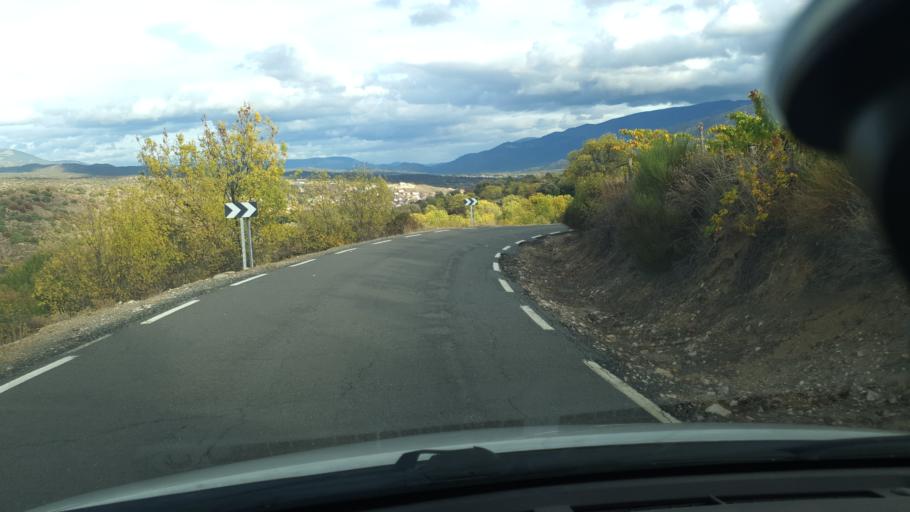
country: ES
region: Castille and Leon
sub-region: Provincia de Avila
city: Burgohondo
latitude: 40.4120
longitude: -4.8083
